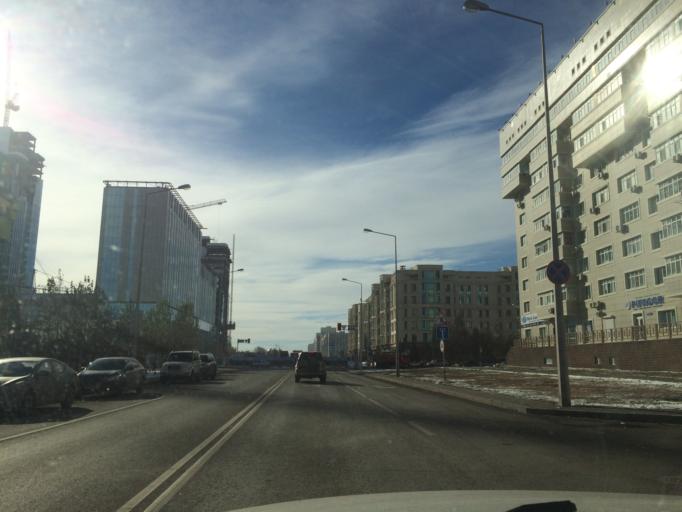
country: KZ
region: Astana Qalasy
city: Astana
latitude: 51.1246
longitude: 71.4270
